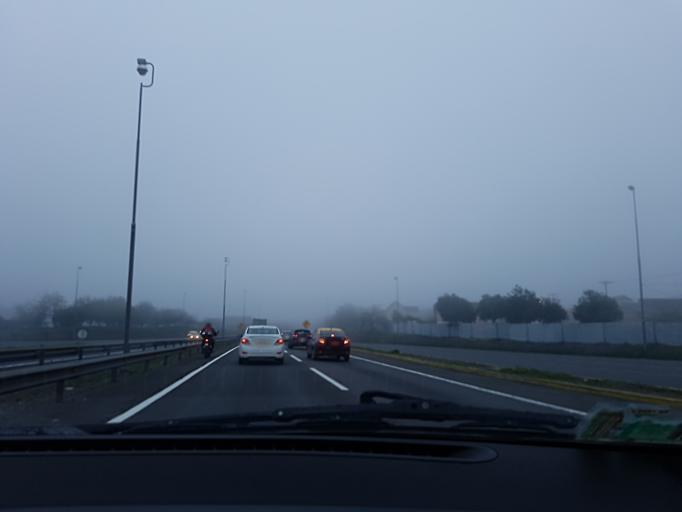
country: CL
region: Santiago Metropolitan
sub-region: Provincia de Santiago
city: Lo Prado
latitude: -33.4872
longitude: -70.7450
